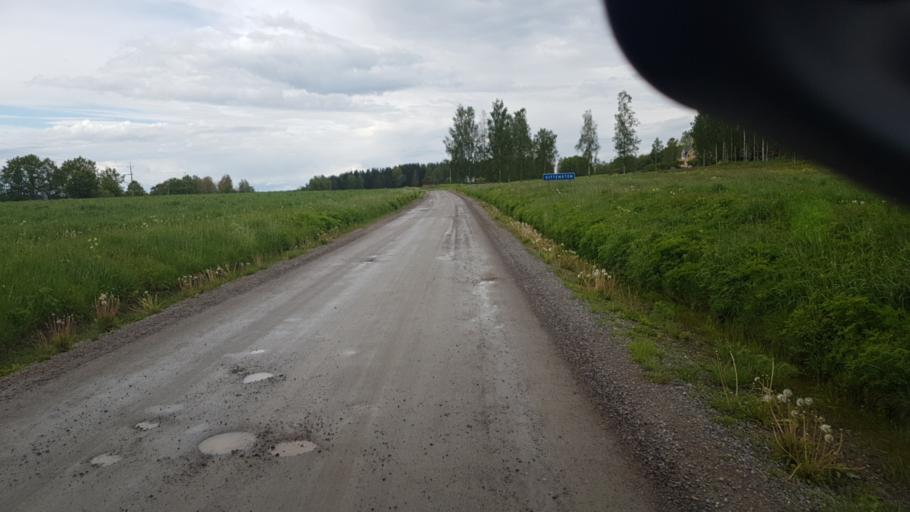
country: SE
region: Vaermland
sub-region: Eda Kommun
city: Amotfors
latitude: 59.8038
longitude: 12.3640
